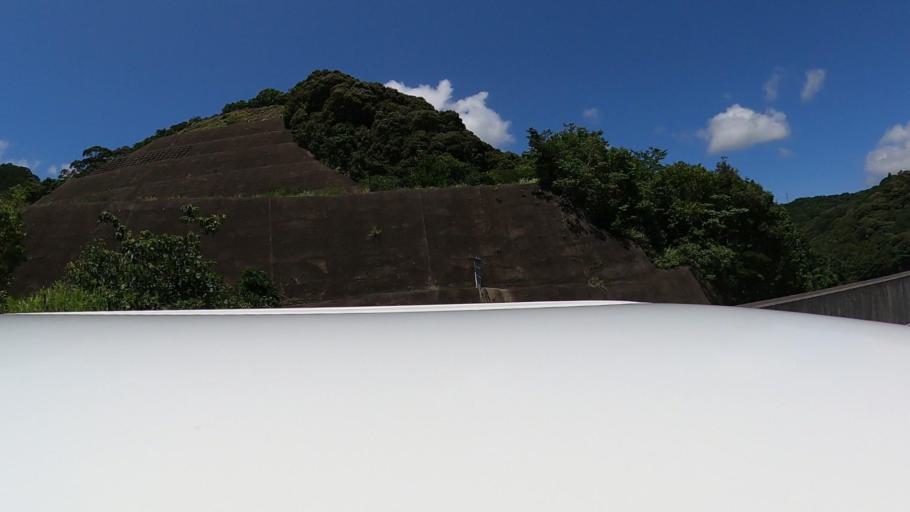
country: JP
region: Miyazaki
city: Nobeoka
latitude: 32.4791
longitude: 131.6317
